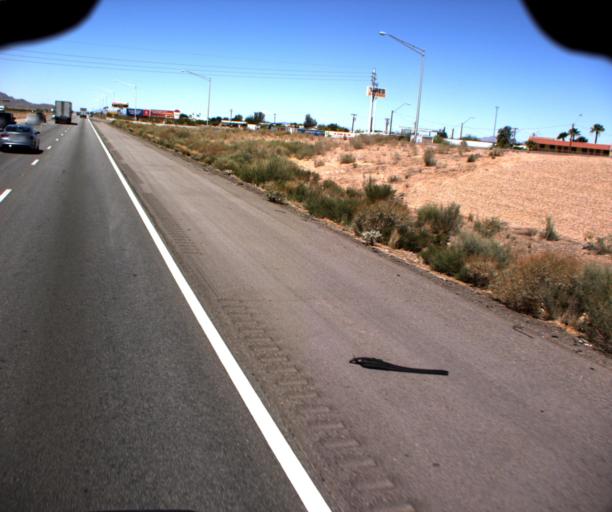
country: US
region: Arizona
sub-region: Pinal County
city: Arizona City
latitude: 32.7782
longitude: -111.6206
